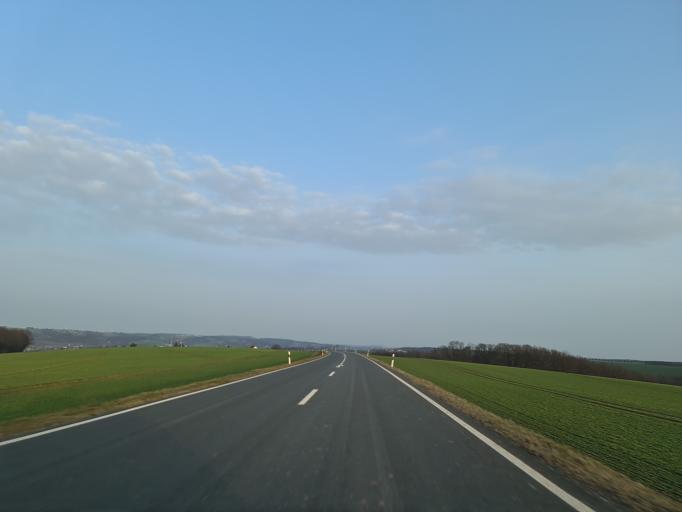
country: DE
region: Thuringia
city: Hartmannsdorf
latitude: 50.9253
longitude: 11.9742
